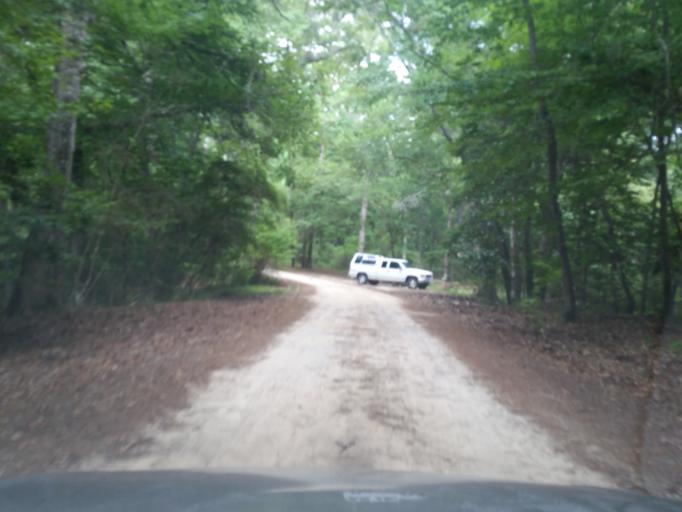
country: US
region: Alabama
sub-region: Baldwin County
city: Spanish Fort
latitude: 30.7422
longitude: -87.9211
